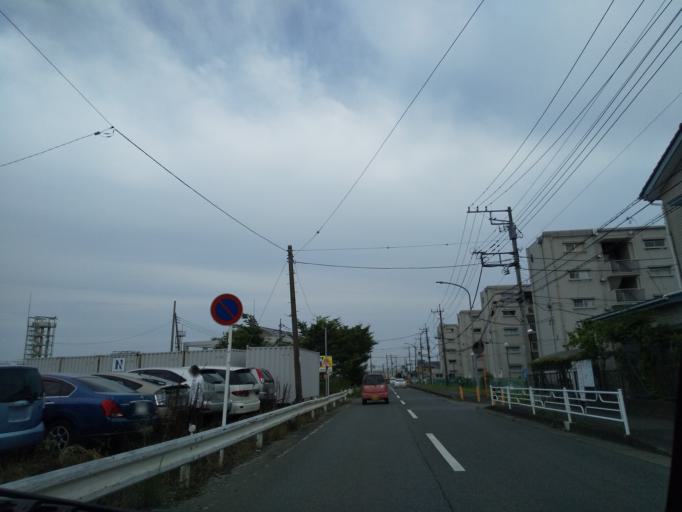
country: JP
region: Kanagawa
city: Atsugi
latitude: 35.4744
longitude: 139.3536
